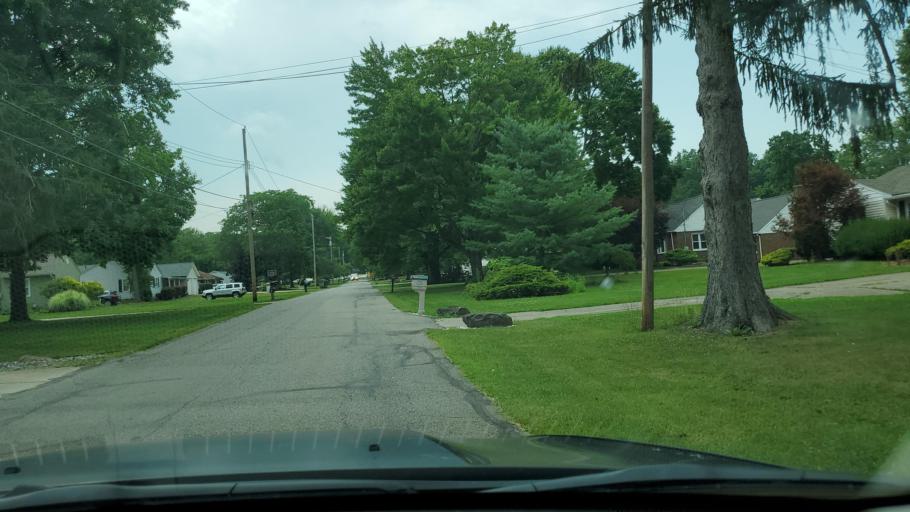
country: US
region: Ohio
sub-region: Trumbull County
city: Bolindale
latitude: 41.2248
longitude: -80.7681
